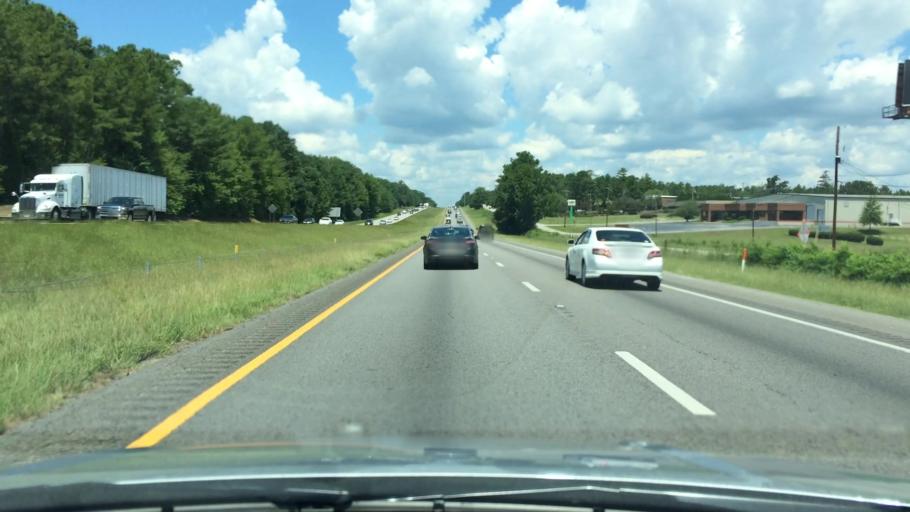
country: US
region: South Carolina
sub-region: Lexington County
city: Irmo
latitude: 34.1103
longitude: -81.1864
